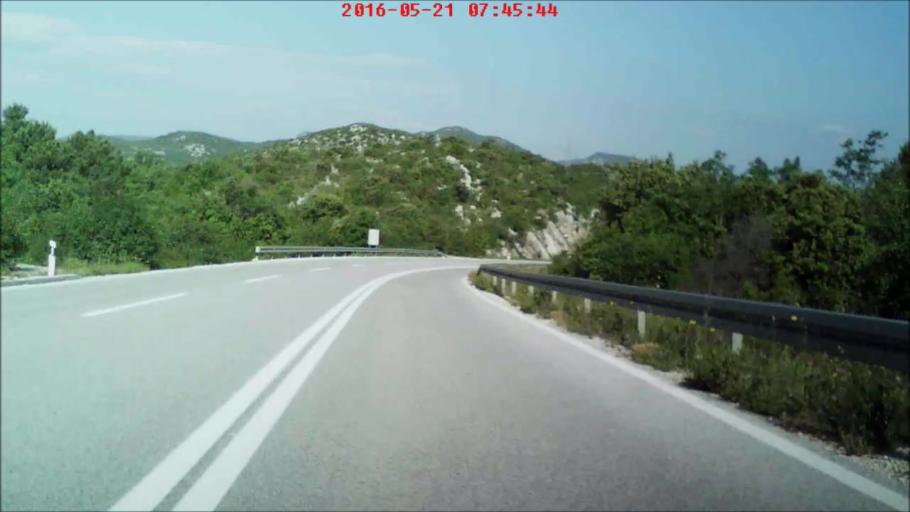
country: HR
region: Dubrovacko-Neretvanska
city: Ston
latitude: 42.8238
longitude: 17.7605
